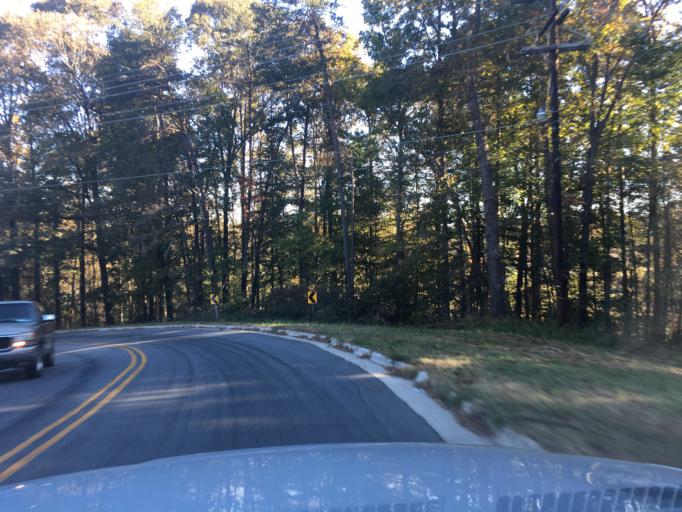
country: US
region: North Carolina
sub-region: Catawba County
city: Hickory
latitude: 35.7259
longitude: -81.3141
